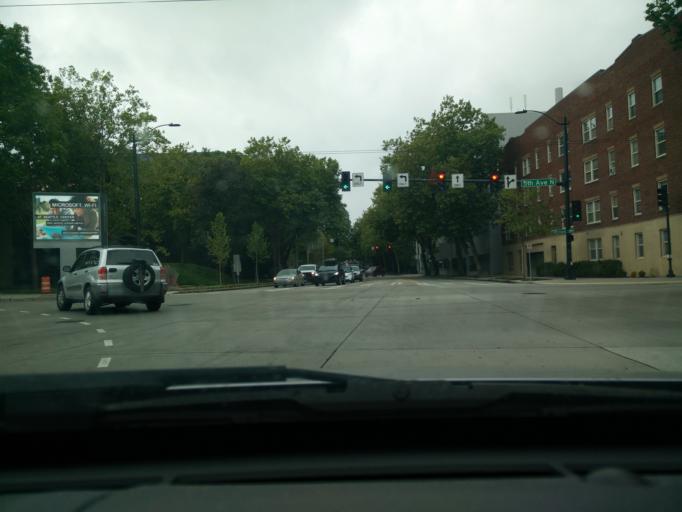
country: US
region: Washington
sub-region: King County
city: Seattle
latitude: 47.6245
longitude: -122.3473
